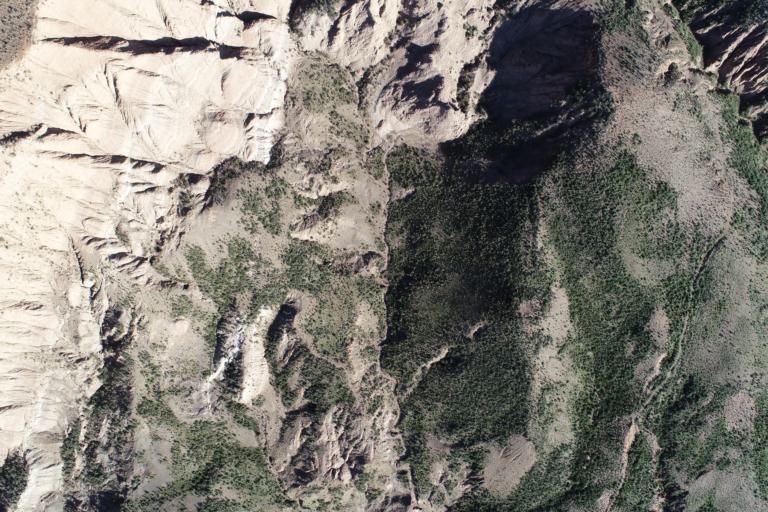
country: BO
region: La Paz
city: Curahuara de Carangas
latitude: -17.3027
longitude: -68.4960
